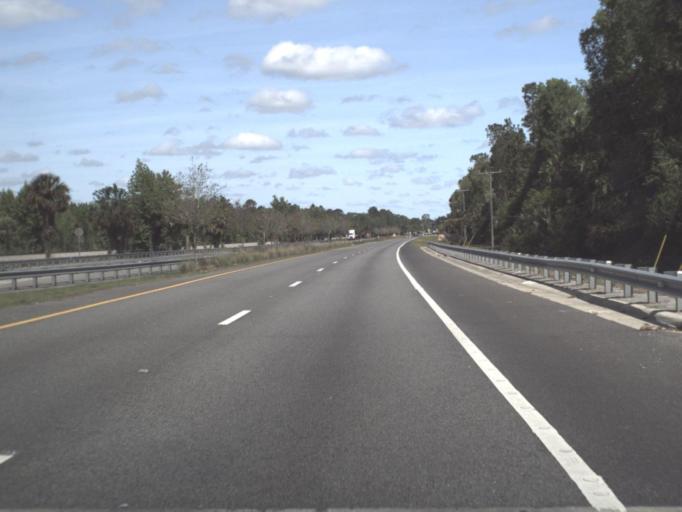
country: US
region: Florida
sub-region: Flagler County
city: Bunnell
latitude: 29.4518
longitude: -81.2457
